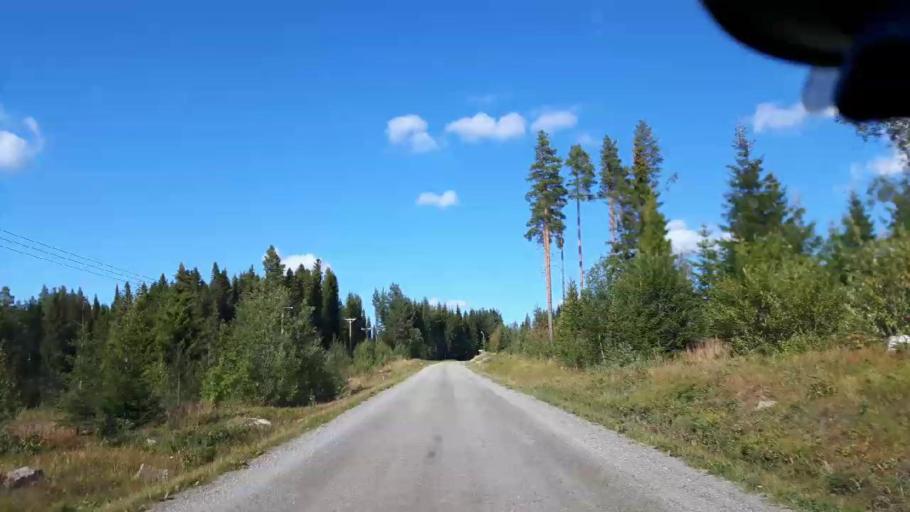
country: SE
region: Jaemtland
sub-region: Ragunda Kommun
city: Hammarstrand
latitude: 63.4393
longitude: 15.9485
